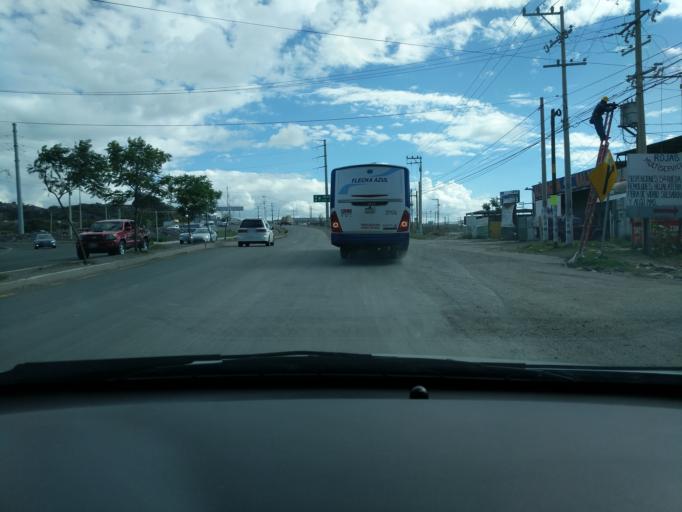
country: MX
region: Queretaro
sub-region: El Marques
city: General Lazaro Cardenas (El Colorado)
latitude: 20.5741
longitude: -100.2586
